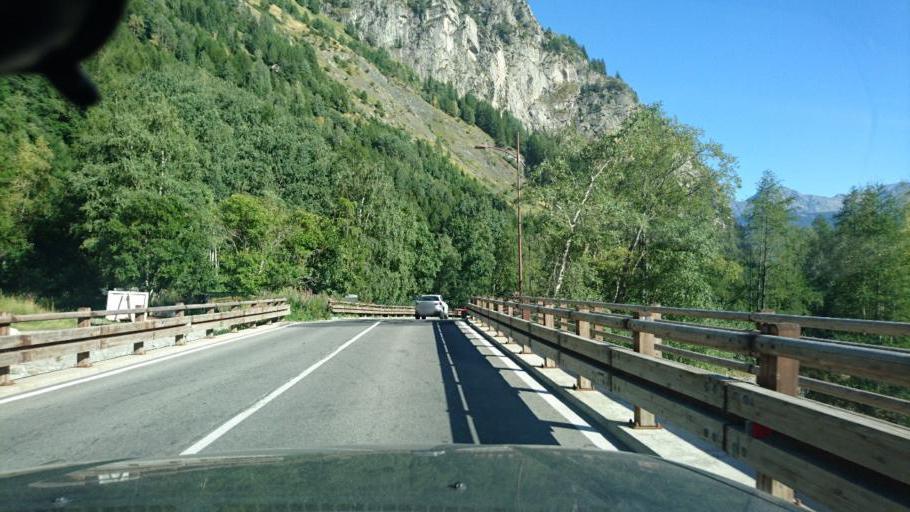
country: IT
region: Aosta Valley
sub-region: Valle d'Aosta
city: Courmayeur
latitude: 45.8123
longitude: 6.9634
